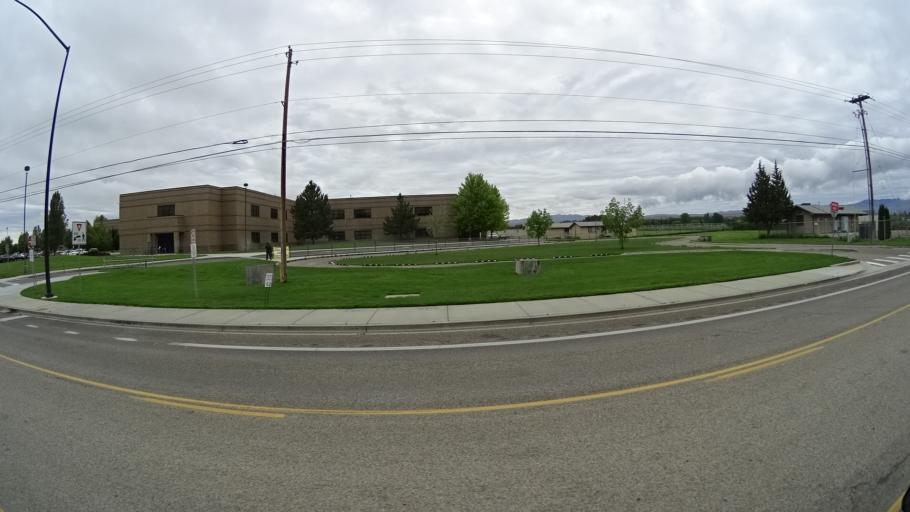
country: US
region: Idaho
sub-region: Ada County
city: Eagle
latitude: 43.7063
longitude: -116.3649
